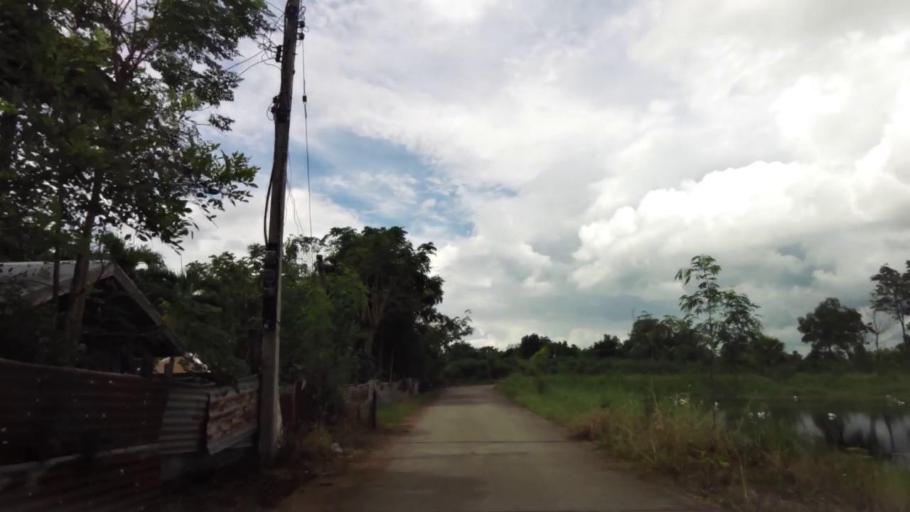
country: TH
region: Nakhon Sawan
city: Phai Sali
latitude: 15.6066
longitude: 100.6543
